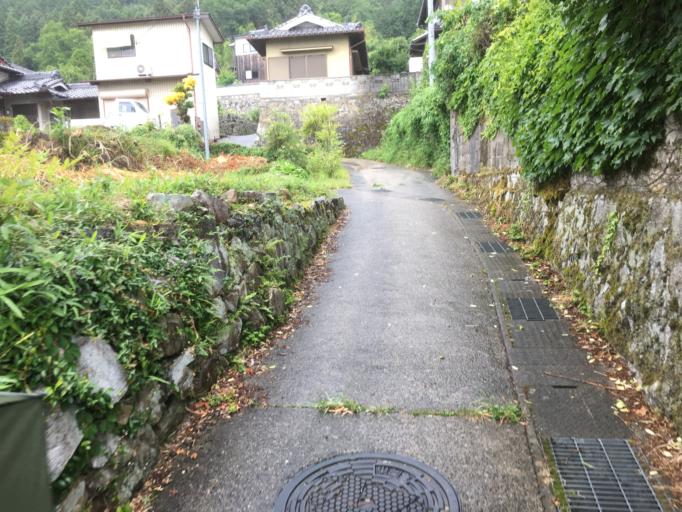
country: JP
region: Kyoto
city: Kameoka
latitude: 35.0109
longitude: 135.6116
